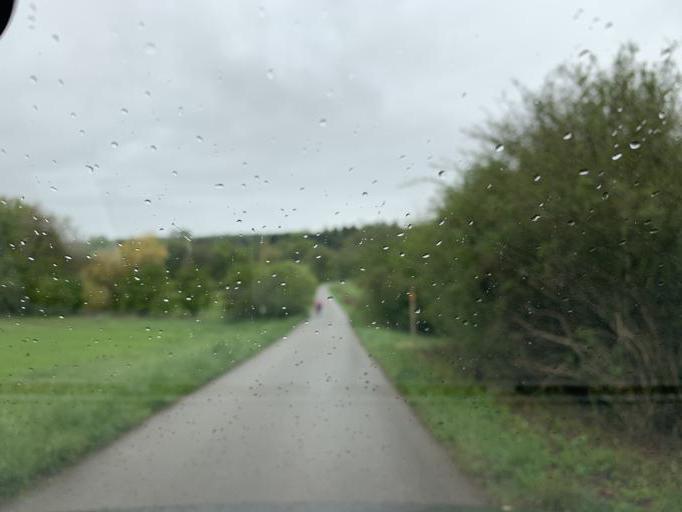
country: CH
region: Schaffhausen
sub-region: Bezirk Schaffhausen
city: Beringen
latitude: 47.7081
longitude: 8.5977
